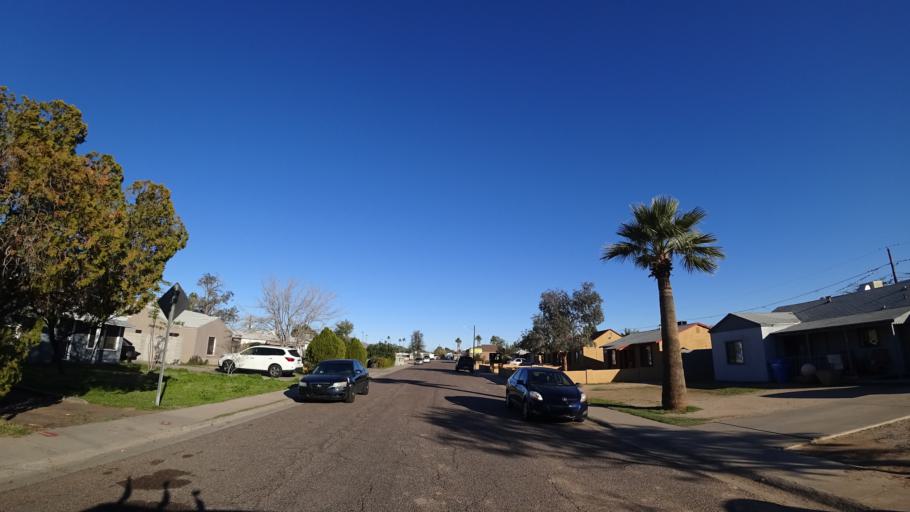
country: US
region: Arizona
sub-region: Maricopa County
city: Phoenix
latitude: 33.4938
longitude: -112.0621
